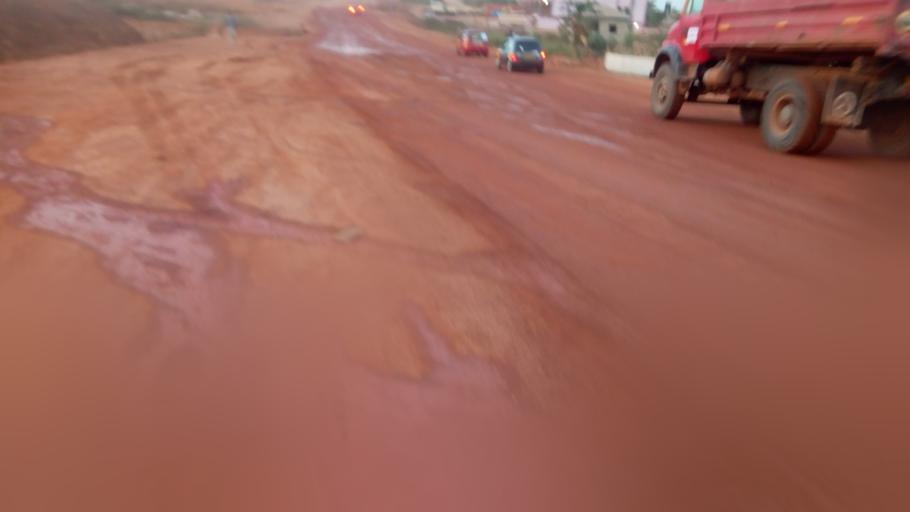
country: GH
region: Ashanti
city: Obuasi
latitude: 6.2267
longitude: -1.6821
